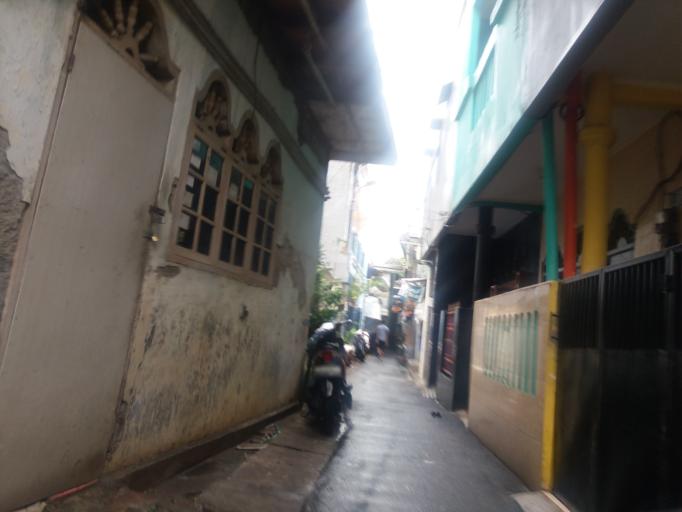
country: ID
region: Jakarta Raya
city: Jakarta
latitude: -6.2161
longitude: 106.8268
